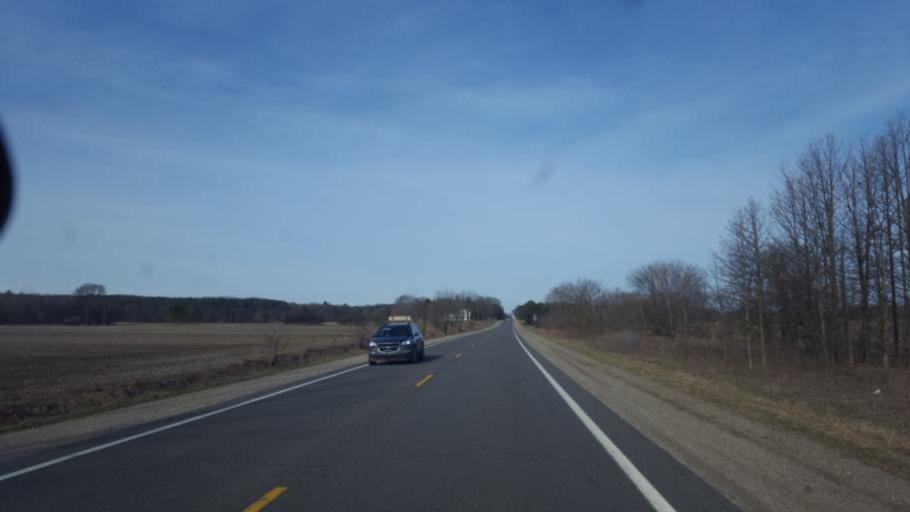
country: US
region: Michigan
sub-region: Montcalm County
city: Lakeview
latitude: 43.4316
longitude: -85.3247
